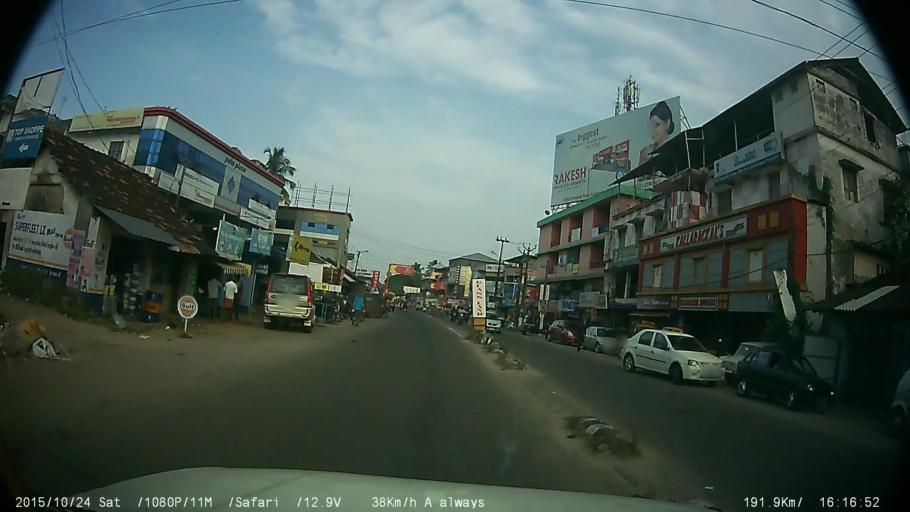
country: IN
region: Kerala
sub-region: Palakkad district
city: Palakkad
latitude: 10.7724
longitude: 76.6715
